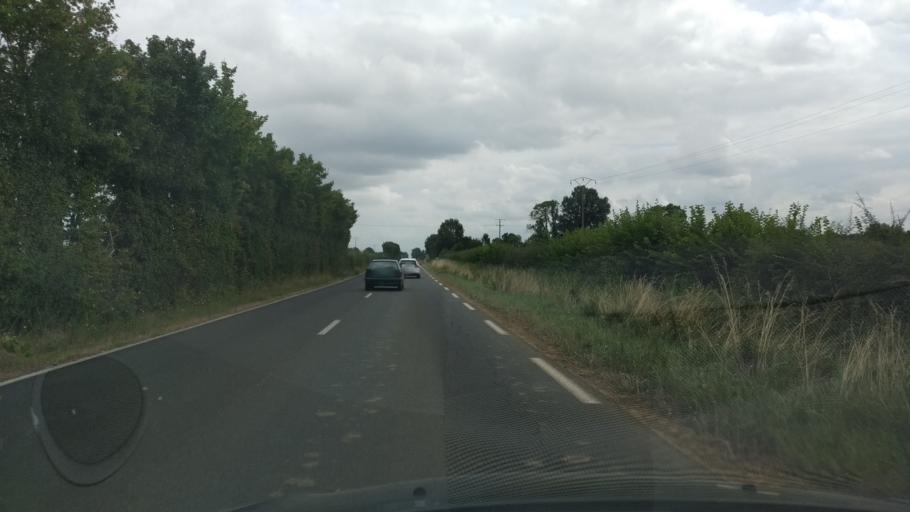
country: FR
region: Poitou-Charentes
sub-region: Departement de la Vienne
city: La Villedieu-du-Clain
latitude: 46.4185
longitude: 0.3836
